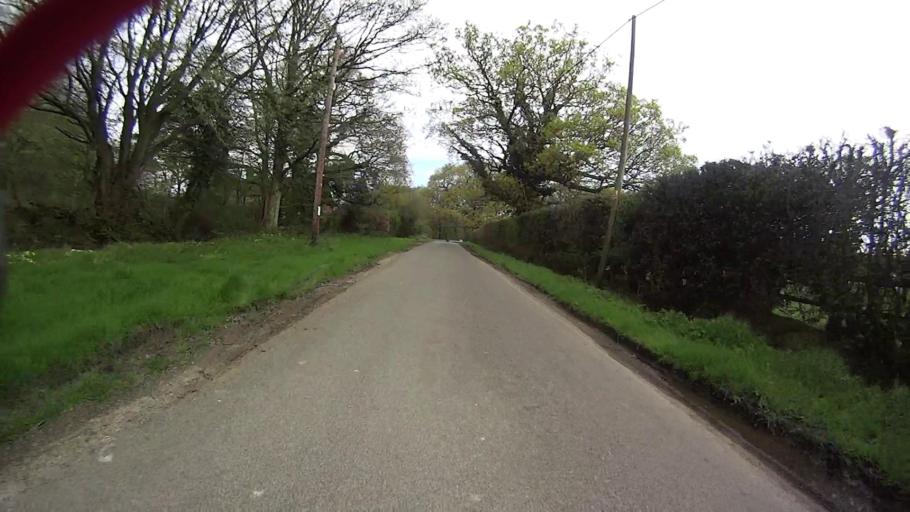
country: GB
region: England
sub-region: West Sussex
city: Bewbush
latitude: 51.1319
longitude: -0.2580
